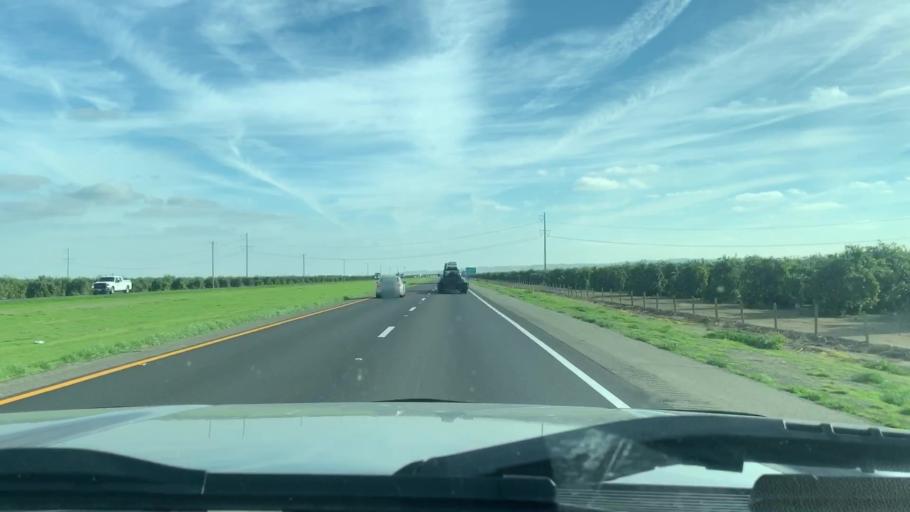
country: US
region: California
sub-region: Fresno County
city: Huron
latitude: 36.1512
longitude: -120.1715
